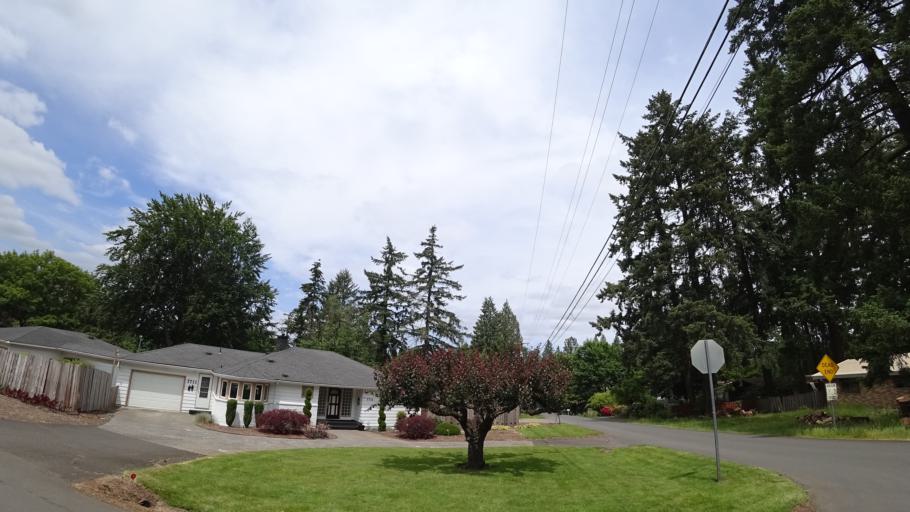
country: US
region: Oregon
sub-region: Washington County
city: Metzger
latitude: 45.4477
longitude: -122.7567
